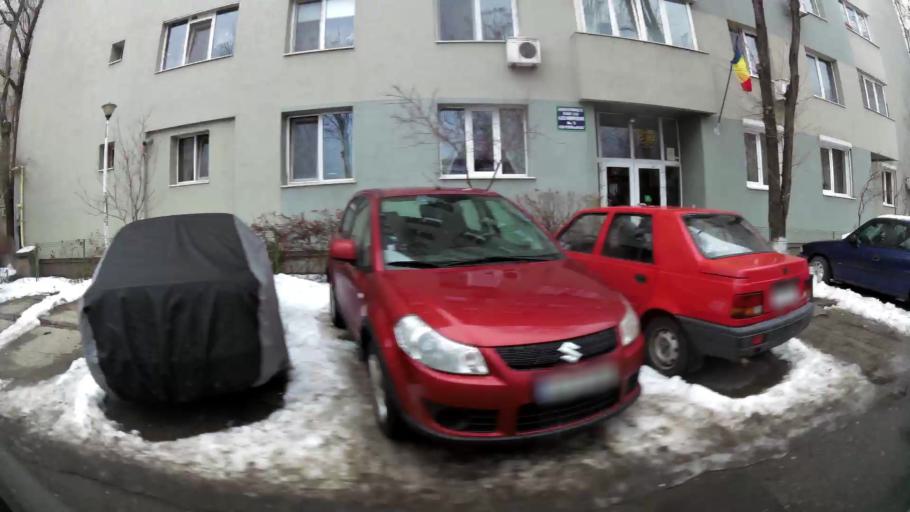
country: RO
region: Bucuresti
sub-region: Municipiul Bucuresti
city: Bucuresti
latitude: 44.4169
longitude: 26.0484
